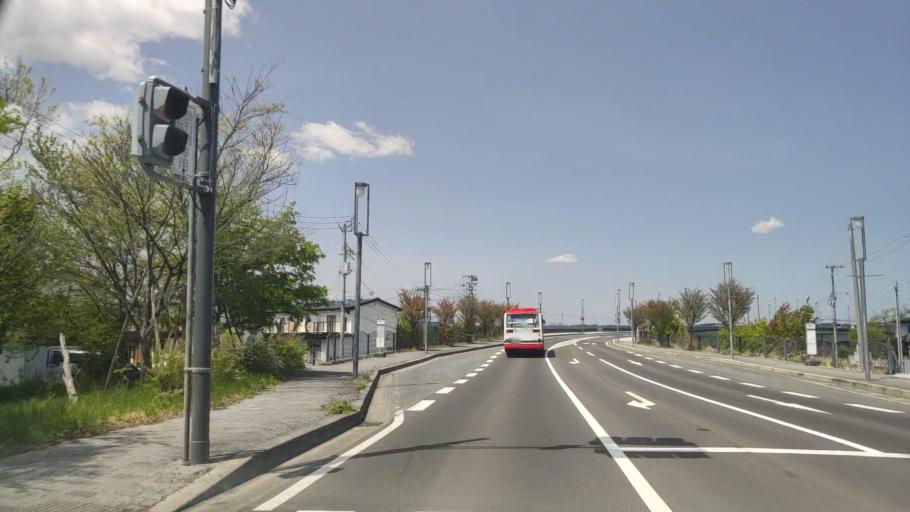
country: JP
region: Aomori
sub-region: Hachinohe Shi
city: Uchimaru
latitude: 40.4993
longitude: 141.4452
